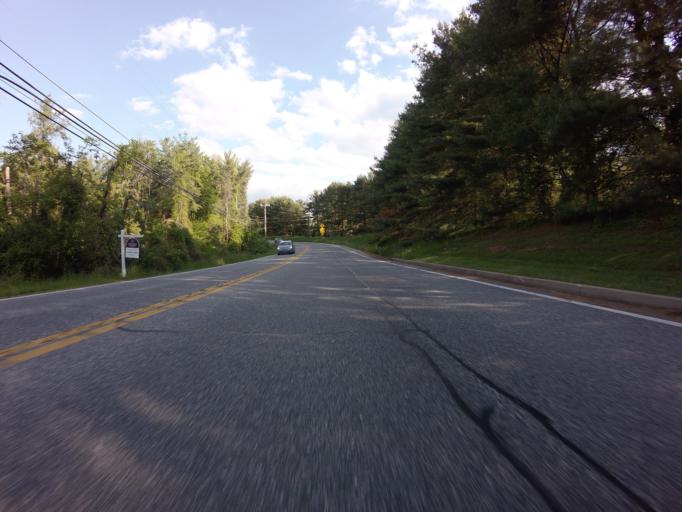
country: US
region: Maryland
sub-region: Baltimore County
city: Cockeysville
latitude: 39.4697
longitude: -76.7019
